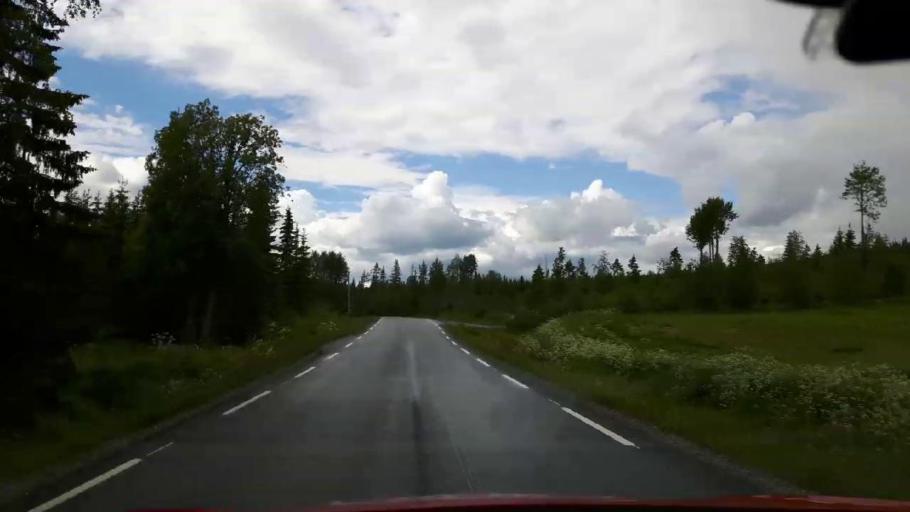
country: NO
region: Nord-Trondelag
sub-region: Lierne
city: Sandvika
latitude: 64.0981
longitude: 14.0332
